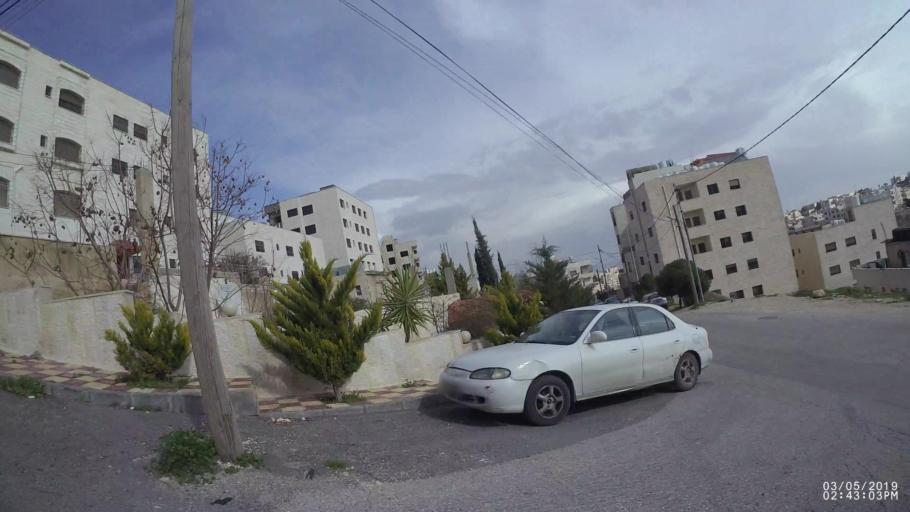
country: JO
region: Amman
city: Amman
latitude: 32.0124
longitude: 35.9416
